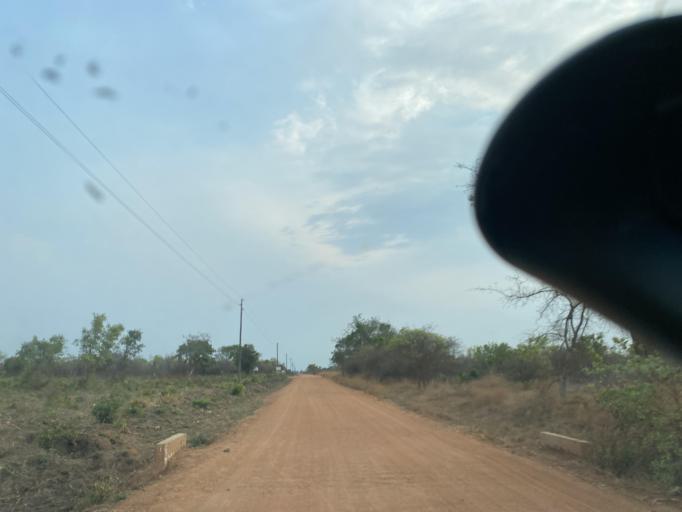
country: ZM
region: Lusaka
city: Chongwe
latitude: -15.2000
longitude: 28.5813
